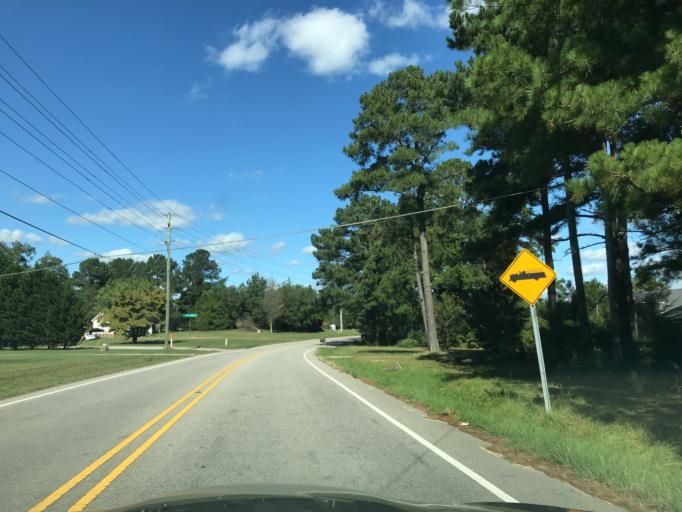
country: US
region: North Carolina
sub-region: Wake County
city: Wake Forest
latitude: 35.9333
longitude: -78.5060
